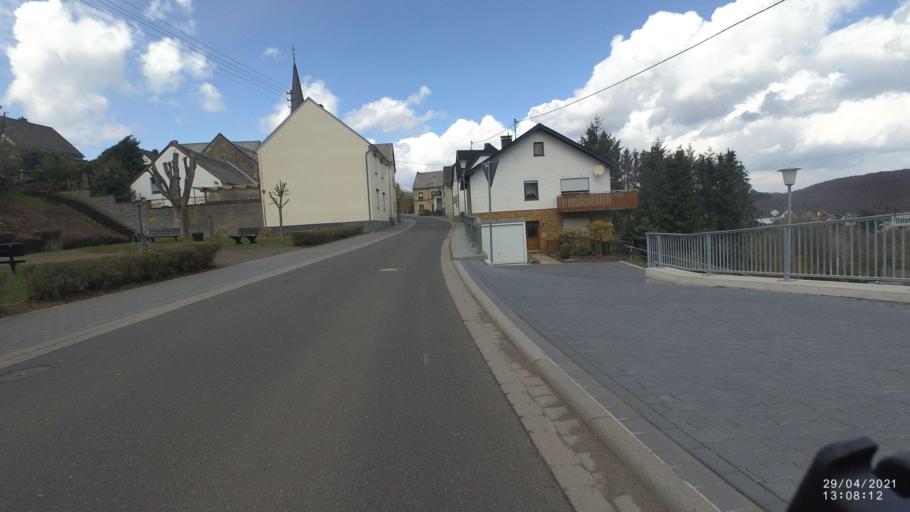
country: DE
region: Rheinland-Pfalz
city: Langenfeld
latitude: 50.3761
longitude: 7.0934
